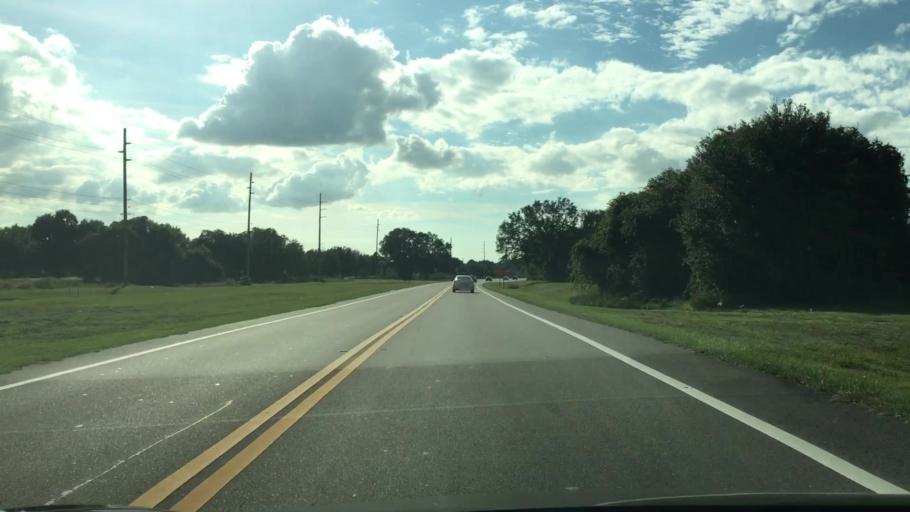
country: US
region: Florida
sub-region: Pasco County
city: Trinity
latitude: 28.1800
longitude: -82.6539
